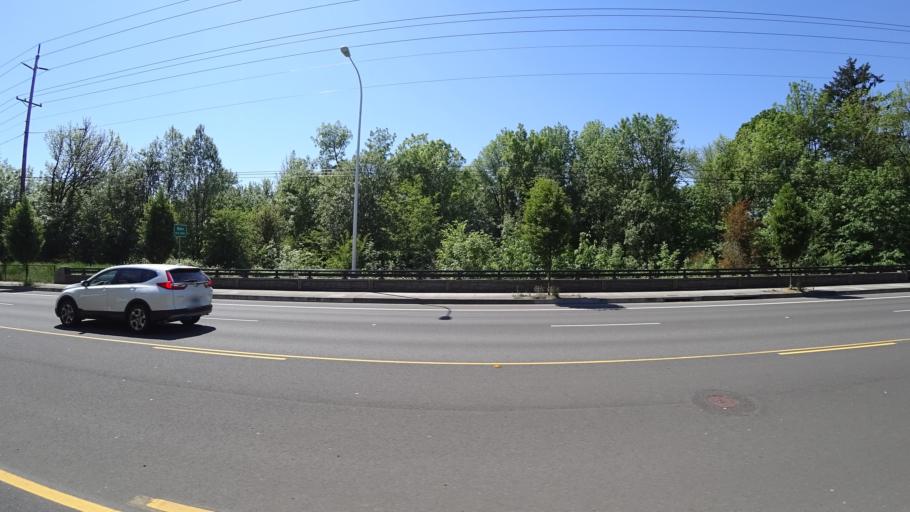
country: US
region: Oregon
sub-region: Washington County
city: Rockcreek
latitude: 45.5285
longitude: -122.8996
